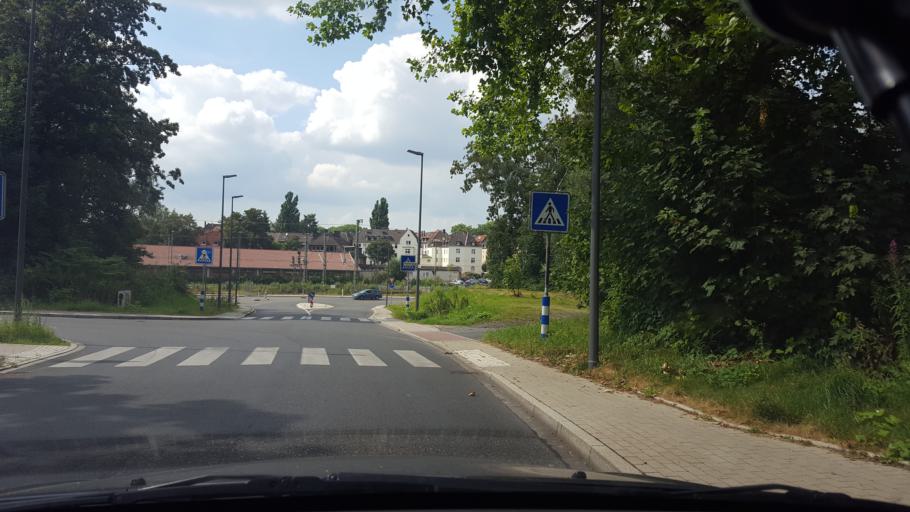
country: DE
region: North Rhine-Westphalia
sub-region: Regierungsbezirk Munster
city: Recklinghausen
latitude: 51.6202
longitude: 7.2074
